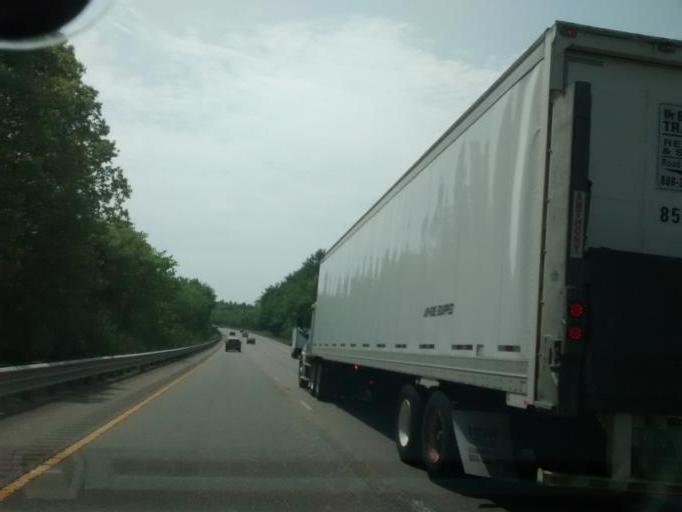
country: US
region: Massachusetts
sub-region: Middlesex County
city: Hopkinton
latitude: 42.2462
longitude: -71.5566
